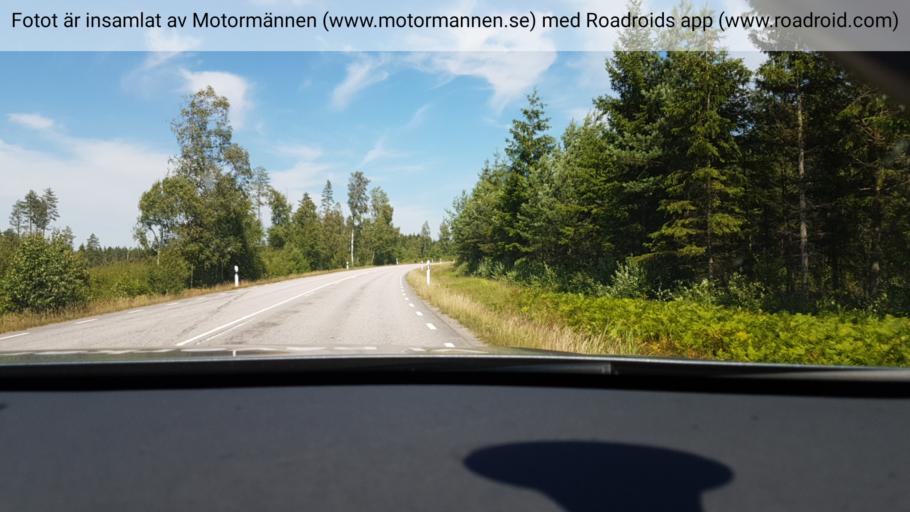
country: SE
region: Vaestra Goetaland
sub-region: Skovde Kommun
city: Stopen
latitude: 58.4443
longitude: 13.9379
